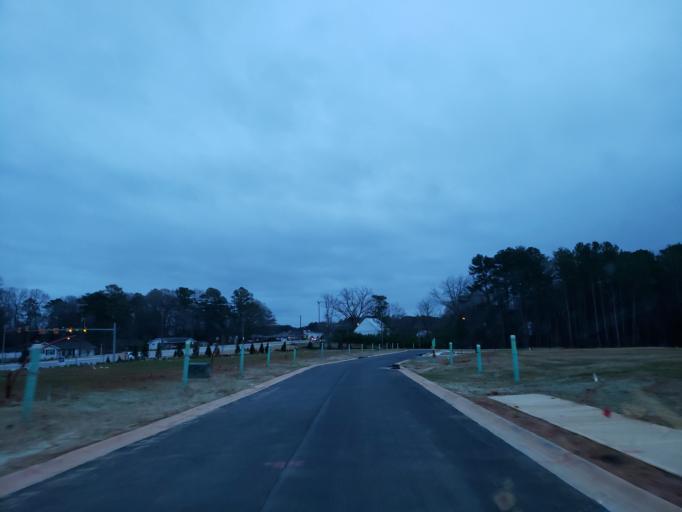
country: US
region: Georgia
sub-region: Cobb County
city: Mableton
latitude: 33.8407
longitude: -84.5794
